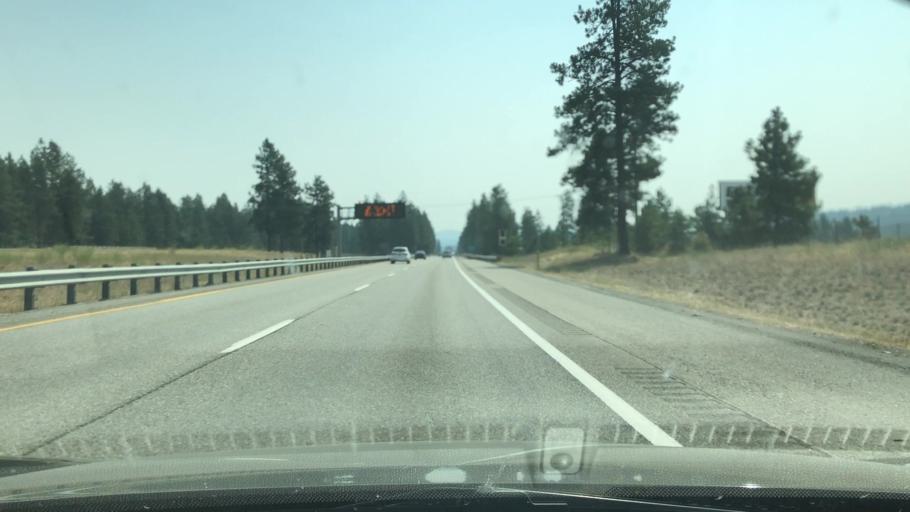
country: US
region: Idaho
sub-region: Kootenai County
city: Coeur d'Alene
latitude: 47.7077
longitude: -116.8530
